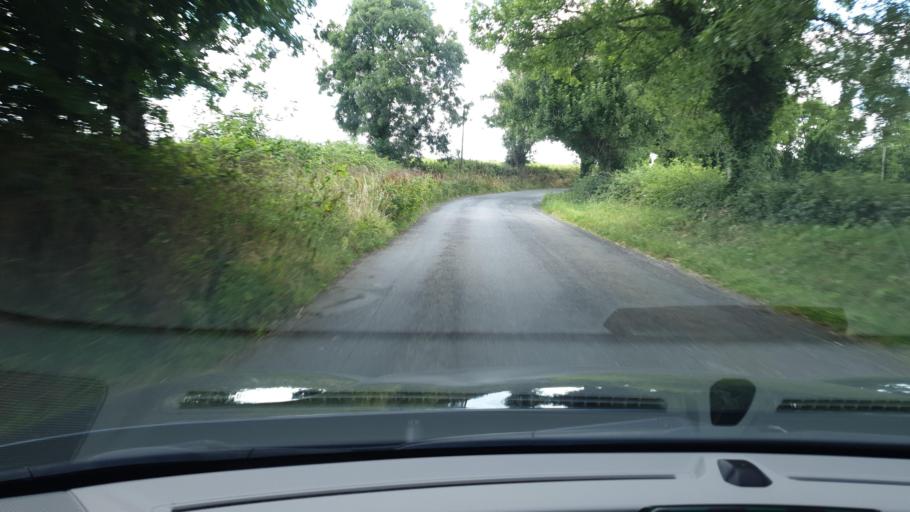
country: IE
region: Leinster
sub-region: An Mhi
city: Newtown Trim
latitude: 53.5459
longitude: -6.6889
